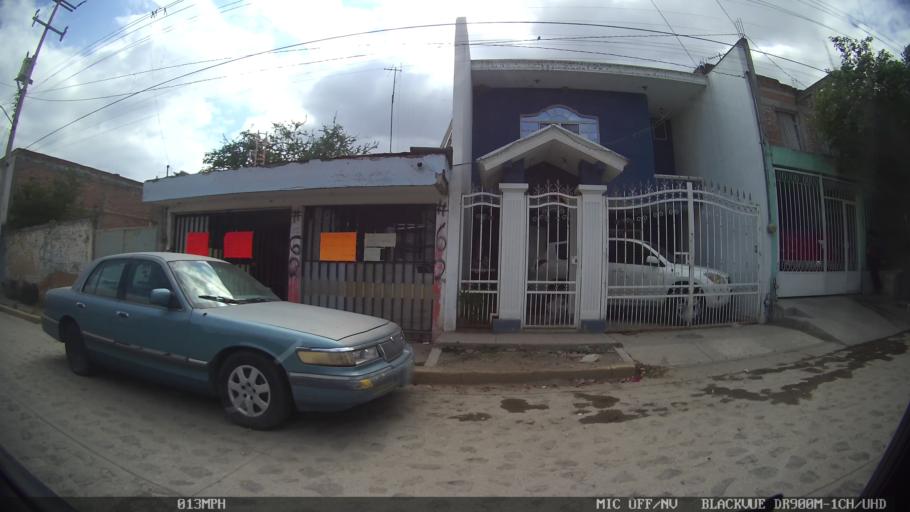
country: MX
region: Jalisco
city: Tlaquepaque
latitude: 20.6755
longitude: -103.2522
